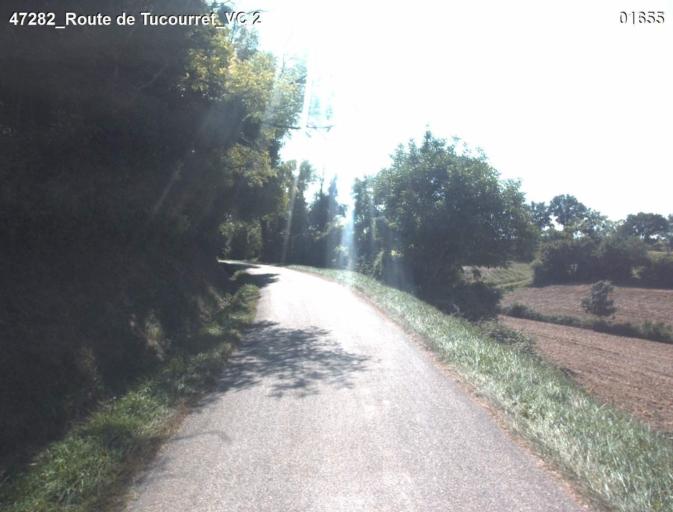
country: FR
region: Aquitaine
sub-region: Departement du Lot-et-Garonne
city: Laplume
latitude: 44.1032
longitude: 0.4875
